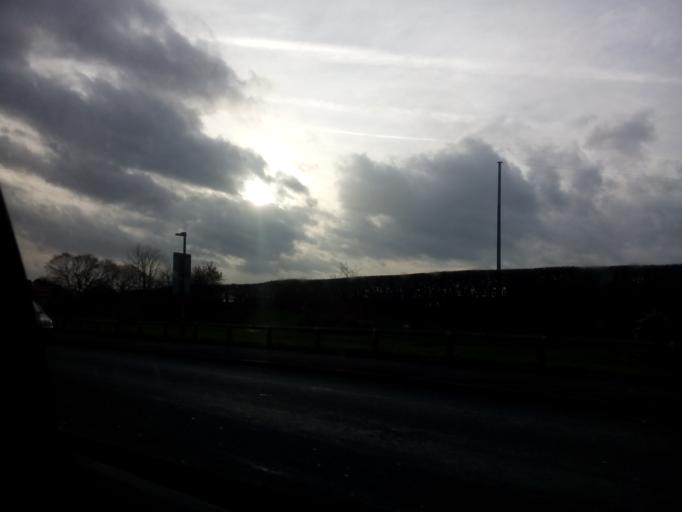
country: GB
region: England
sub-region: Worcestershire
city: Bromsgrove
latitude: 52.3620
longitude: -2.0465
